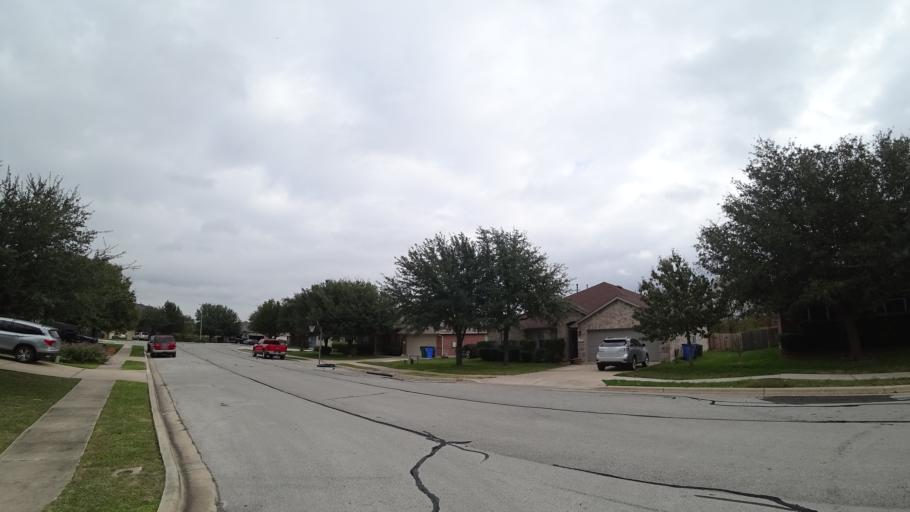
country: US
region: Texas
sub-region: Travis County
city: Pflugerville
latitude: 30.4403
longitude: -97.6019
